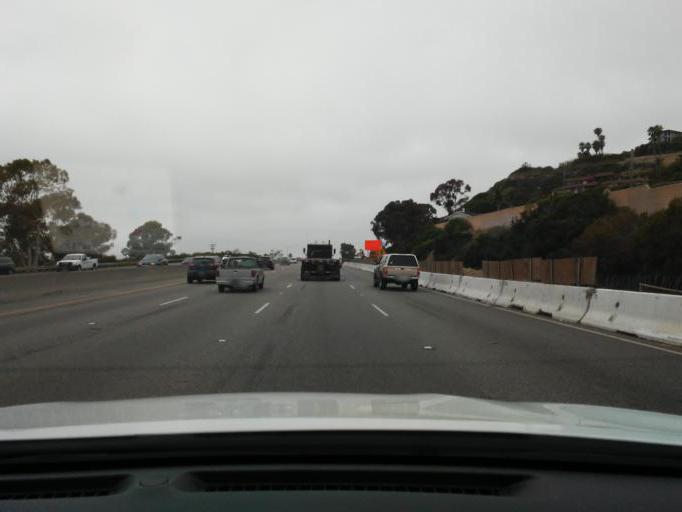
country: US
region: California
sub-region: Orange County
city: San Clemente
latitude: 33.4198
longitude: -117.6057
